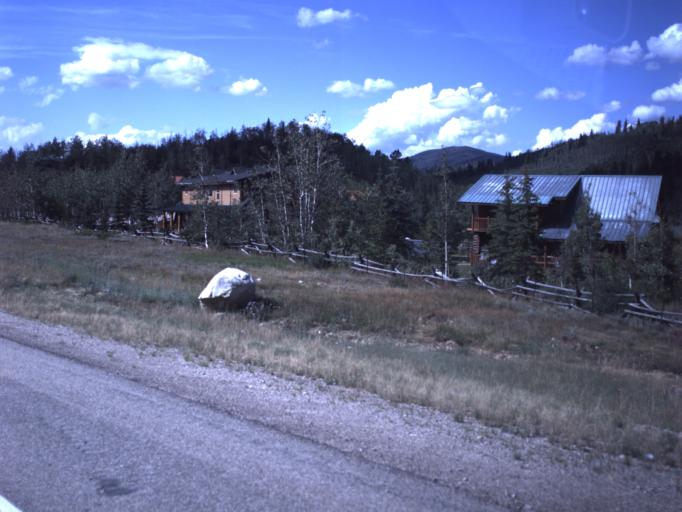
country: US
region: Utah
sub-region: Wasatch County
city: Heber
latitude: 40.3029
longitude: -111.2567
